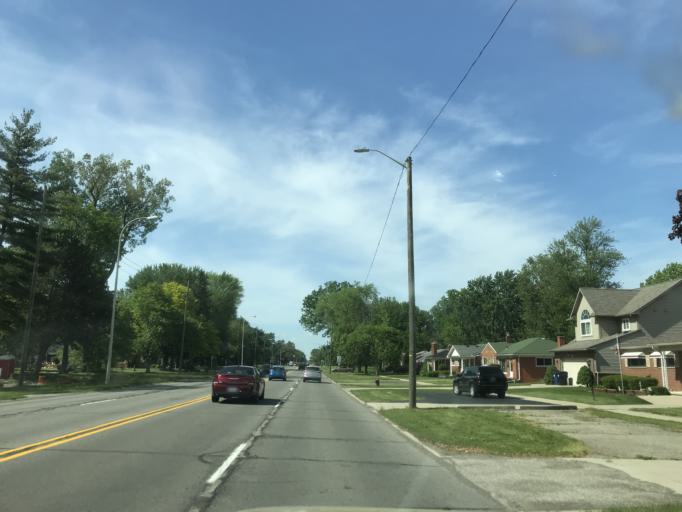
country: US
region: Michigan
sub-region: Wayne County
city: Redford
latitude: 42.3593
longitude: -83.3129
